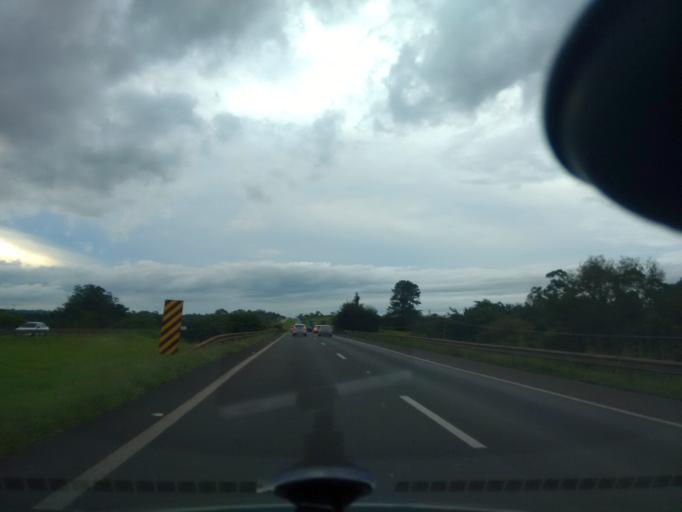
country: BR
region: Sao Paulo
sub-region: Rio Claro
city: Rio Claro
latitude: -22.3914
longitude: -47.6013
